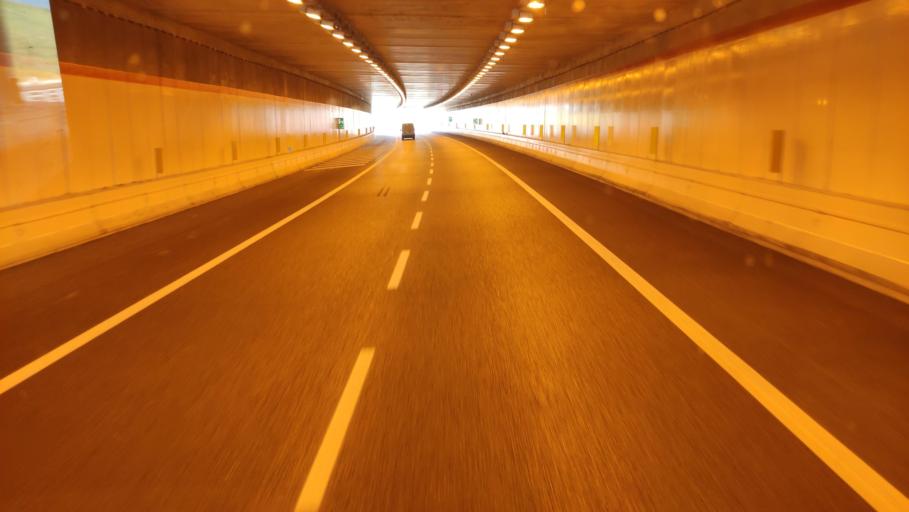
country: IT
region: Veneto
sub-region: Provincia di Treviso
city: Altivole
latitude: 45.7332
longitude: 11.9569
